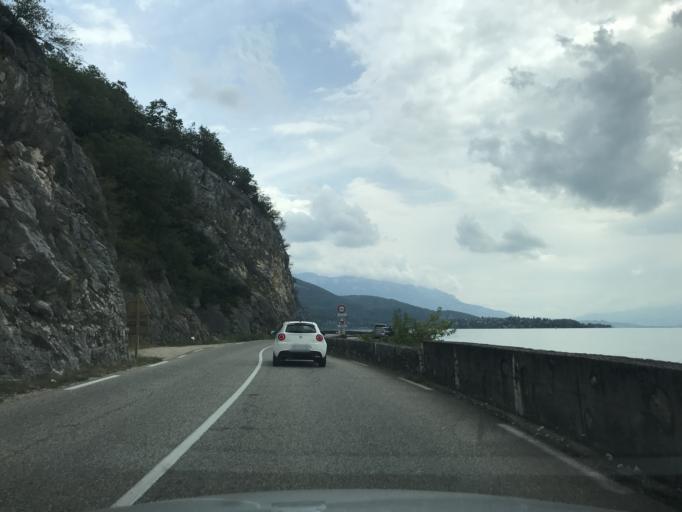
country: FR
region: Rhone-Alpes
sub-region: Departement de la Savoie
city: Brison-Saint-Innocent
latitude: 45.7591
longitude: 5.8708
